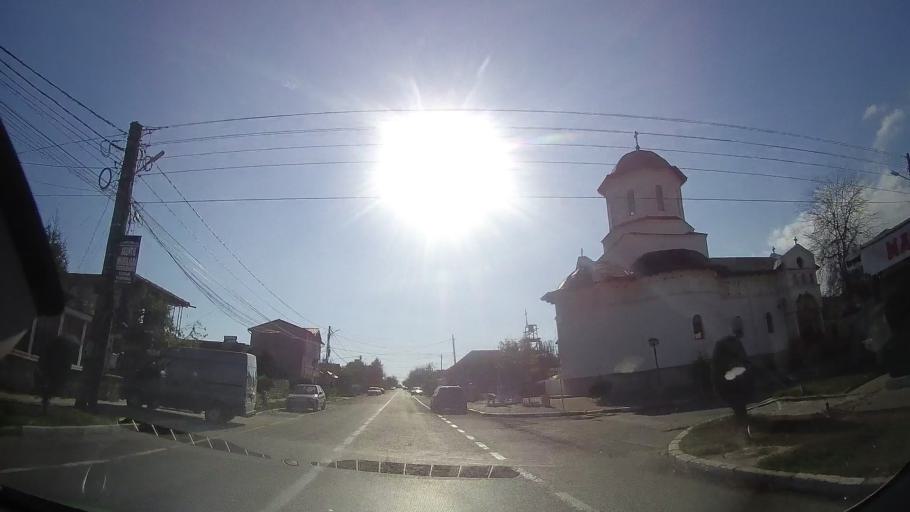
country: RO
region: Constanta
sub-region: Comuna Costinesti
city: Schitu
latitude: 43.9429
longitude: 28.6295
